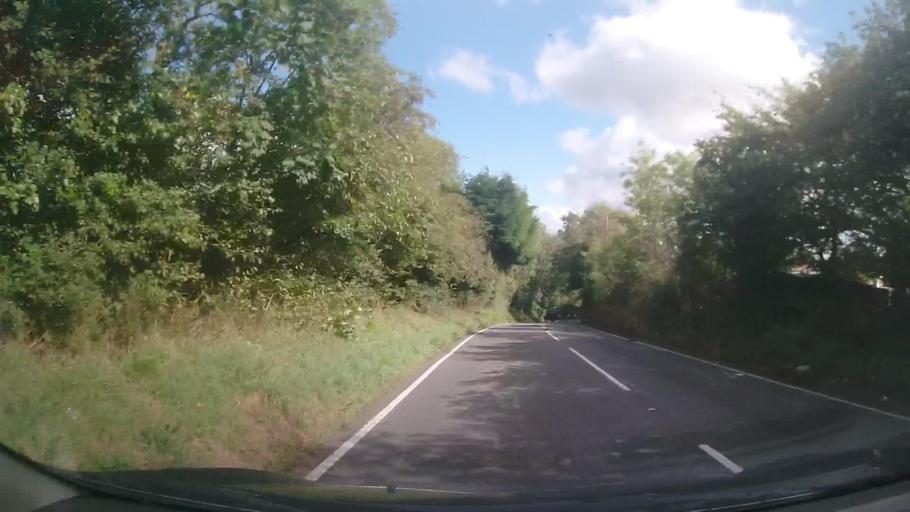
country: GB
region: Wales
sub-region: Pembrokeshire
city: Pembroke
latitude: 51.6832
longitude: -4.8833
